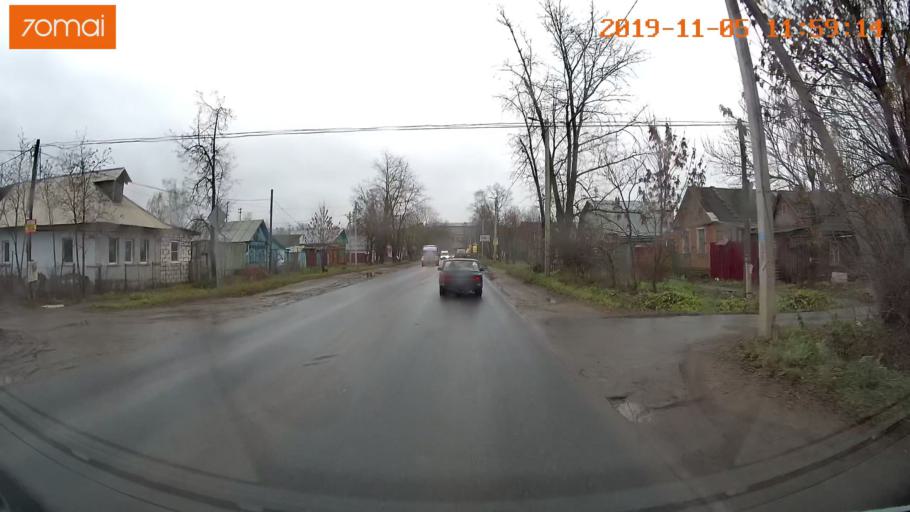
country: RU
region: Ivanovo
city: Kokhma
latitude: 56.9788
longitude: 41.0465
